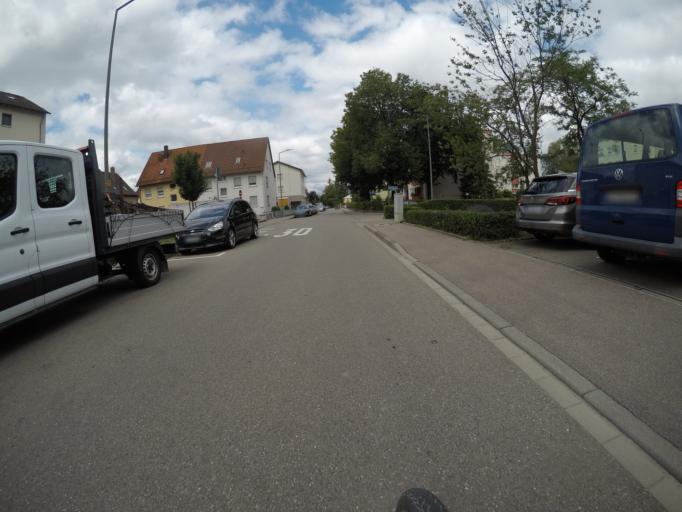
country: DE
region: Baden-Wuerttemberg
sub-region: Regierungsbezirk Stuttgart
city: Eislingen
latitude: 48.6999
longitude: 9.7157
